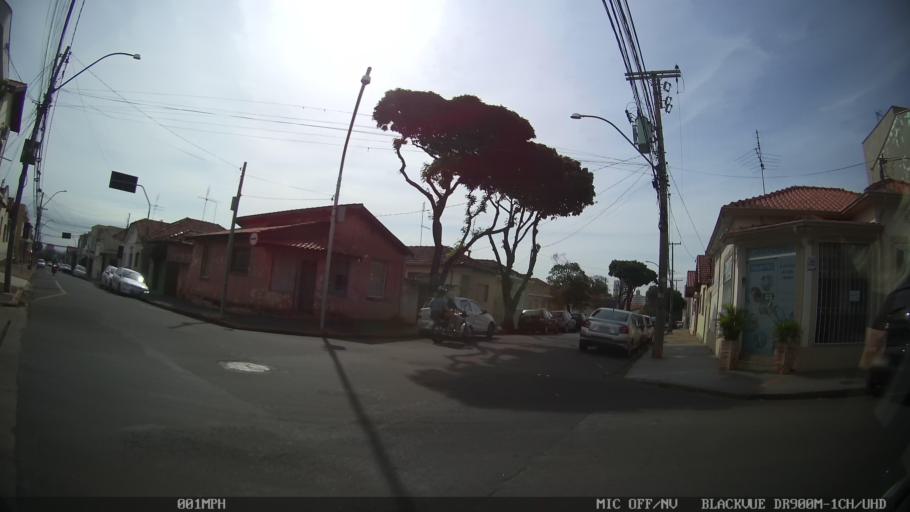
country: BR
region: Sao Paulo
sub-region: Piracicaba
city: Piracicaba
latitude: -22.7373
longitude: -47.6574
